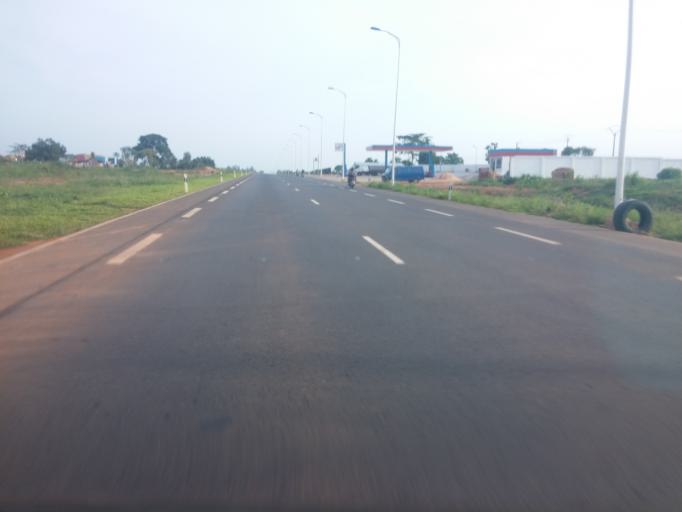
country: TG
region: Maritime
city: Tsevie
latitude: 6.3478
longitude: 1.2133
